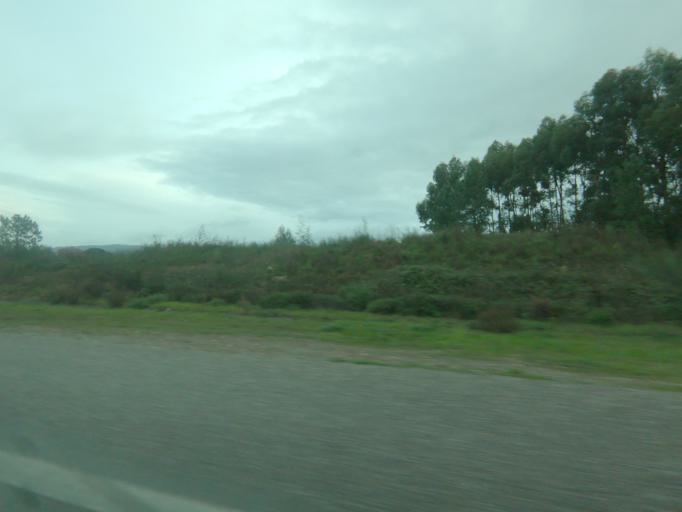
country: PT
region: Viana do Castelo
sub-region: Valenca
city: Valenza
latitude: 41.9644
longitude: -8.6683
